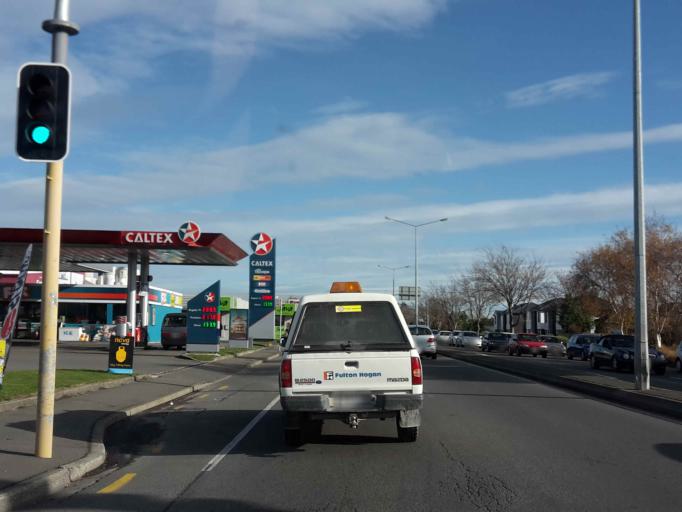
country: NZ
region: Canterbury
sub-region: Christchurch City
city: Christchurch
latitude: -43.5375
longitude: 172.5965
